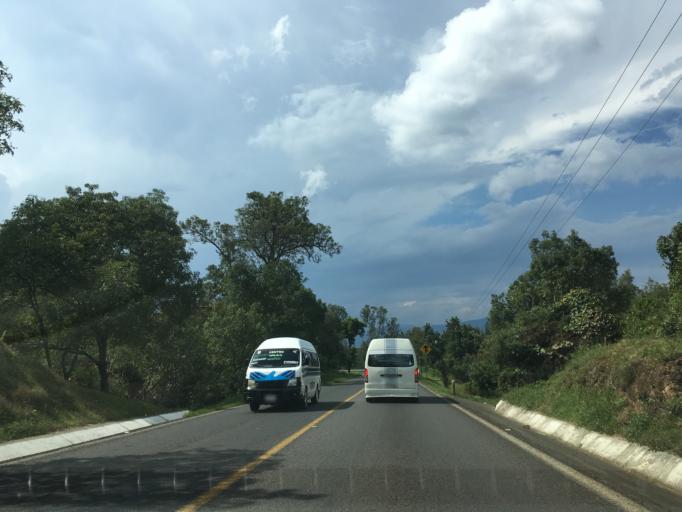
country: MX
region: Michoacan
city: Patzcuaro
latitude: 19.5460
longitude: -101.5916
